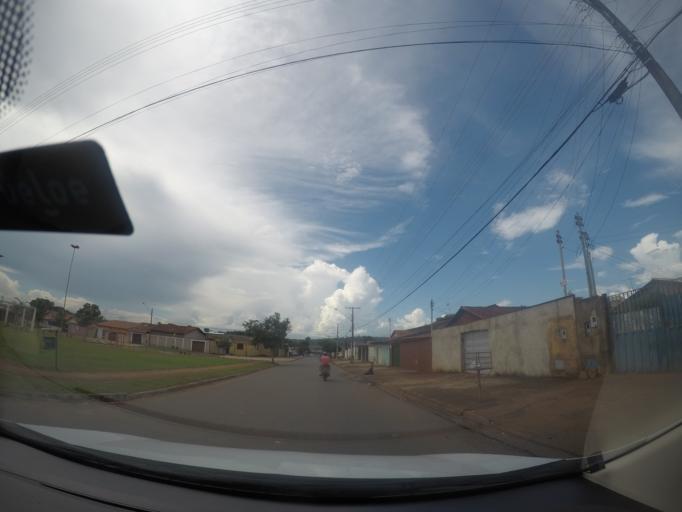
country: BR
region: Goias
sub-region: Goiania
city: Goiania
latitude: -16.6984
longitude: -49.3562
